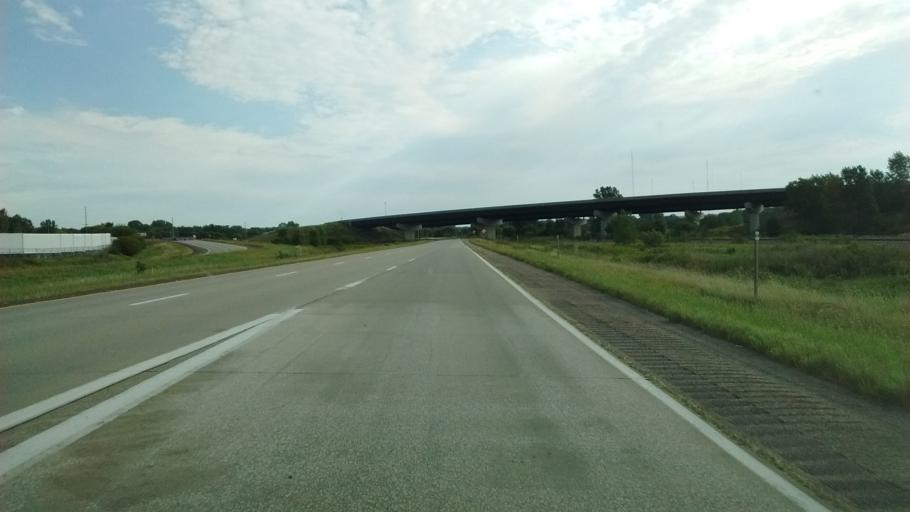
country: US
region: Iowa
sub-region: Woodbury County
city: Sioux City
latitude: 42.5514
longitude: -96.3445
